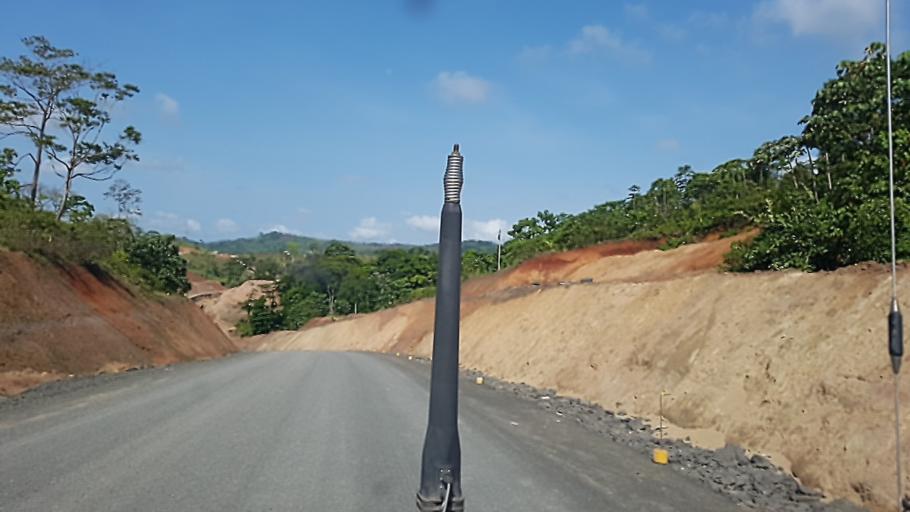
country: NI
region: Atlantico Sur
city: Nueva Guinea
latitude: 11.8056
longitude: -84.1203
